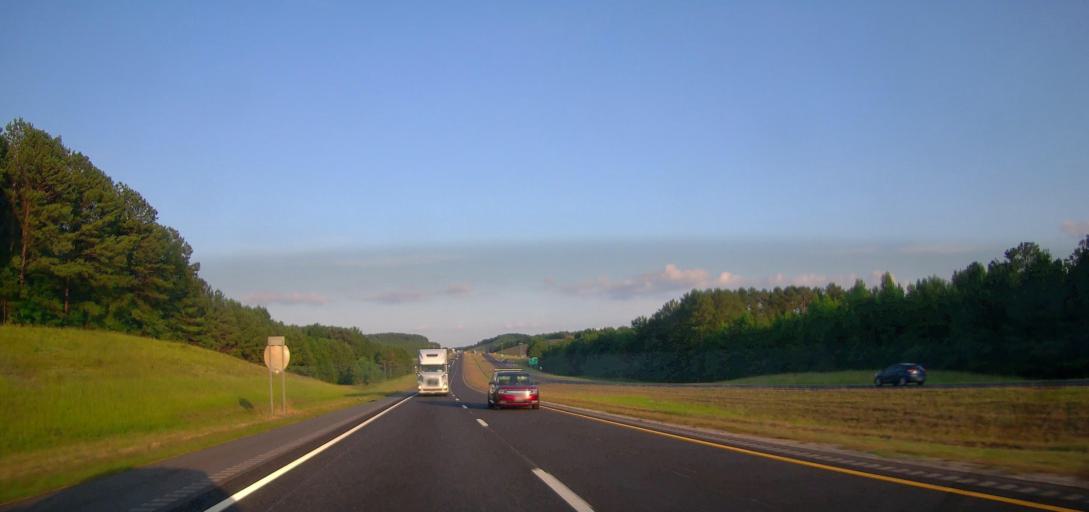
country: US
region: Alabama
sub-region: Marion County
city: Guin
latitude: 34.0174
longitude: -87.8410
